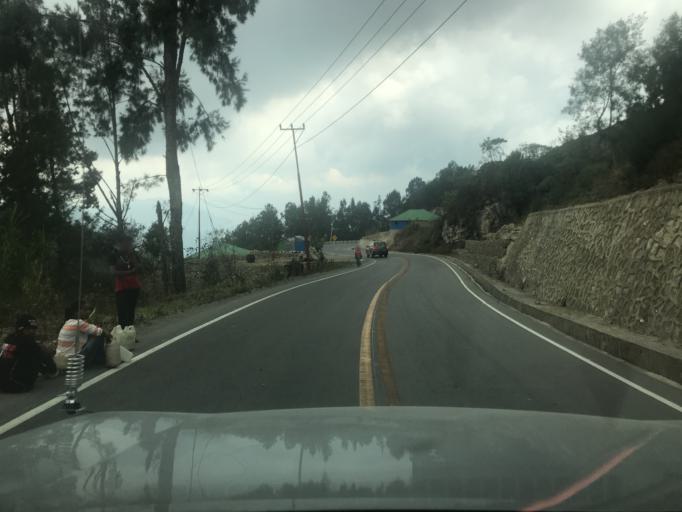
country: TL
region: Manufahi
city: Same
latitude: -8.8861
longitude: 125.6002
